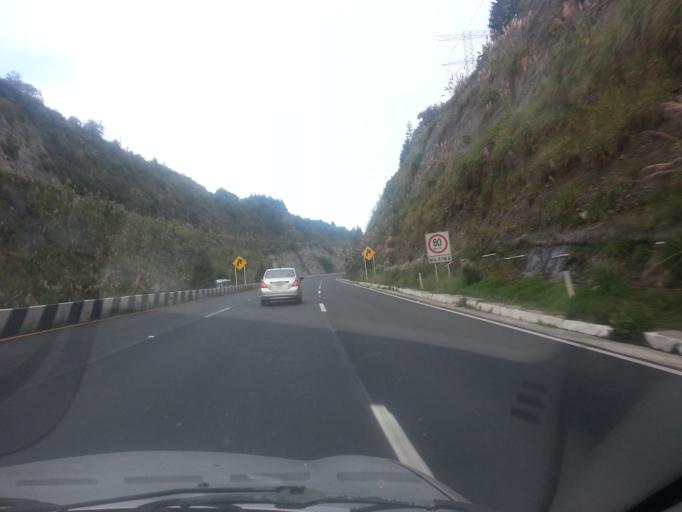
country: MX
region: Mexico City
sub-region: Cuajimalpa de Morelos
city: San Lorenzo Acopilco
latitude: 19.2985
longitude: -99.3483
